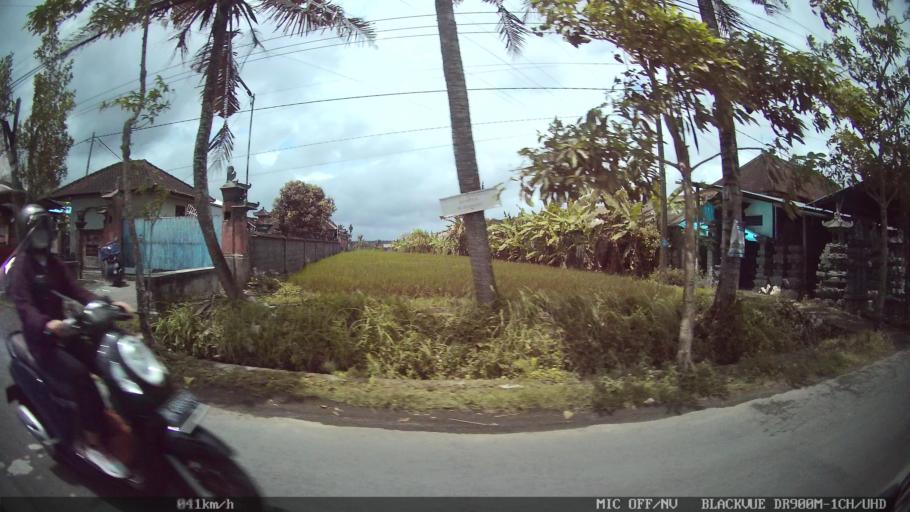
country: ID
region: Bali
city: Banjar Pekenjelodan
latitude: -8.5648
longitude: 115.1853
